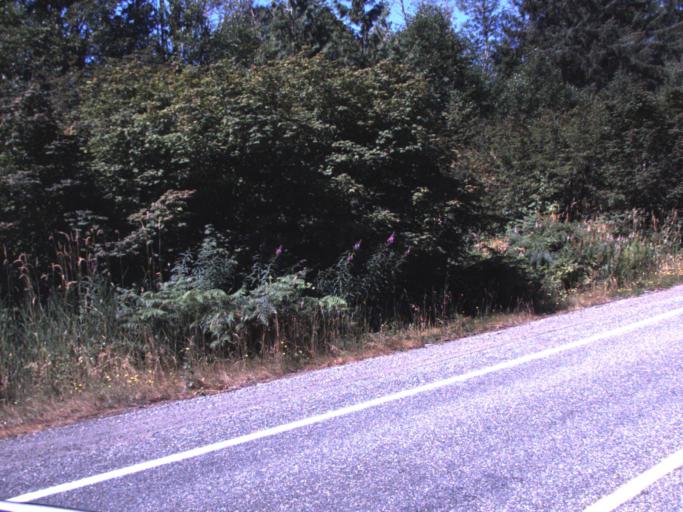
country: US
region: Washington
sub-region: King County
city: Enumclaw
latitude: 47.1556
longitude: -121.8604
